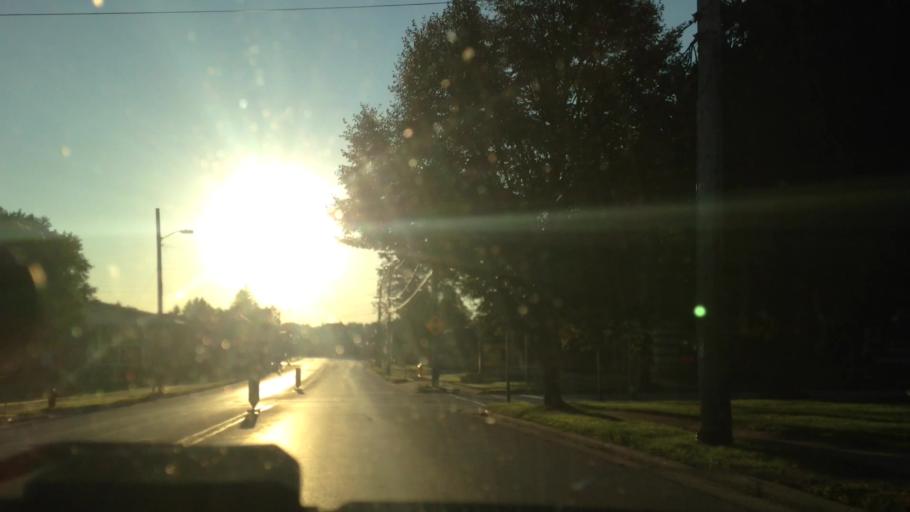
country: US
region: Wisconsin
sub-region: Ozaukee County
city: Saukville
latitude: 43.3819
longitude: -87.9423
